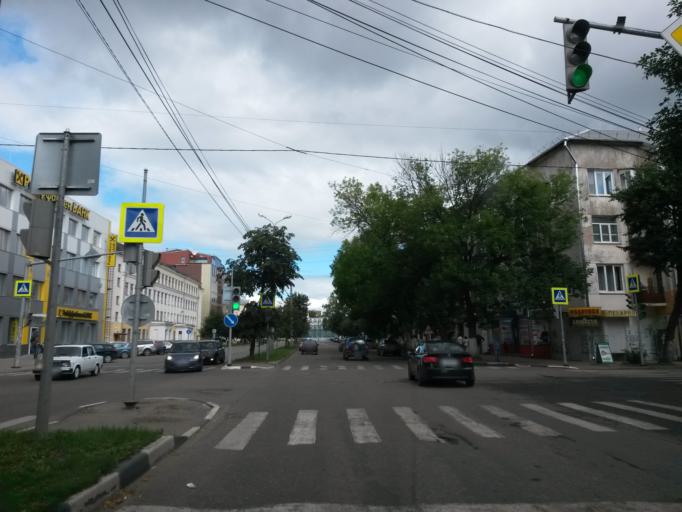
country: RU
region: Jaroslavl
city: Yaroslavl
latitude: 57.6324
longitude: 39.8707
